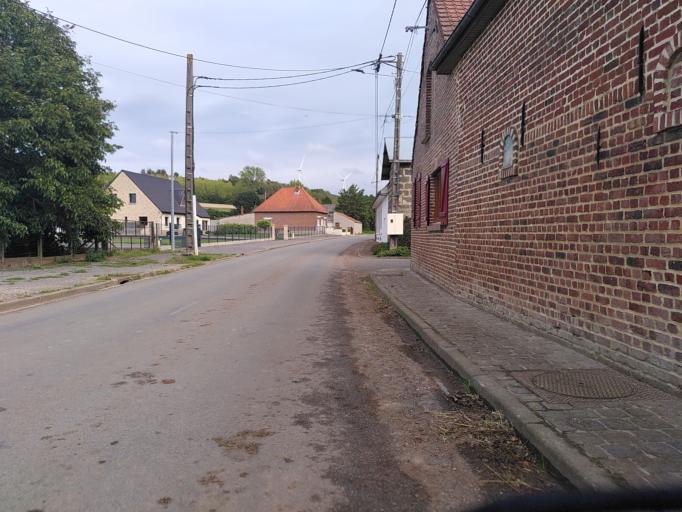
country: FR
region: Nord-Pas-de-Calais
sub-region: Departement du Pas-de-Calais
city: Therouanne
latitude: 50.6019
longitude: 2.1867
